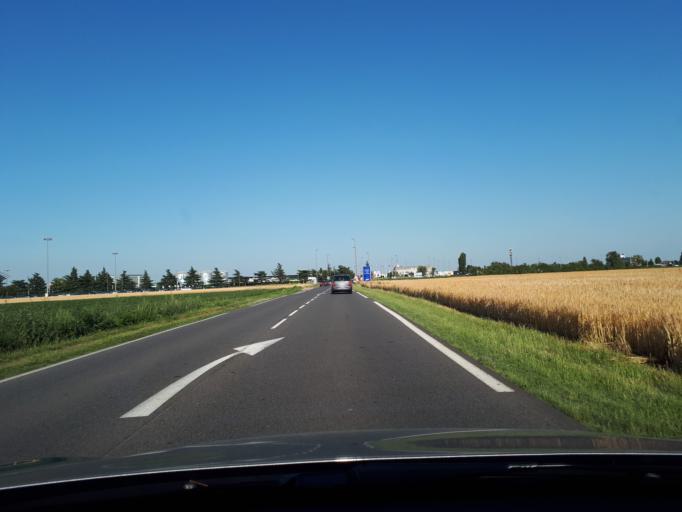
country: FR
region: Rhone-Alpes
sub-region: Departement du Rhone
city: Saint-Laurent-de-Mure
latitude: 45.7182
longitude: 5.0654
